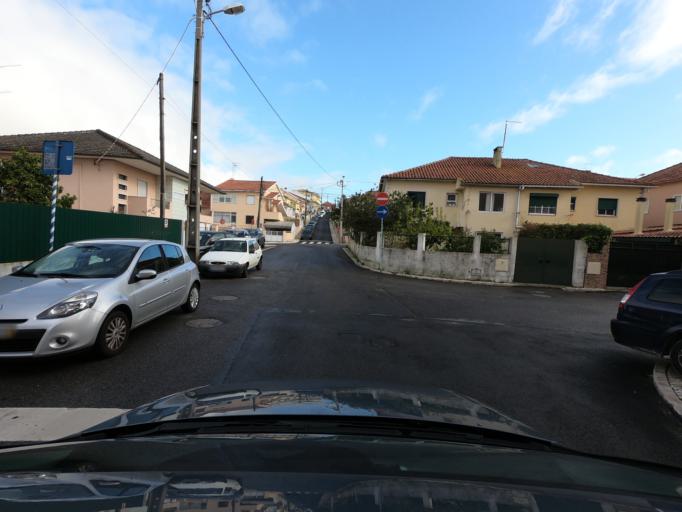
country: PT
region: Lisbon
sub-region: Oeiras
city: Porto Salvo
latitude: 38.7222
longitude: -9.3085
